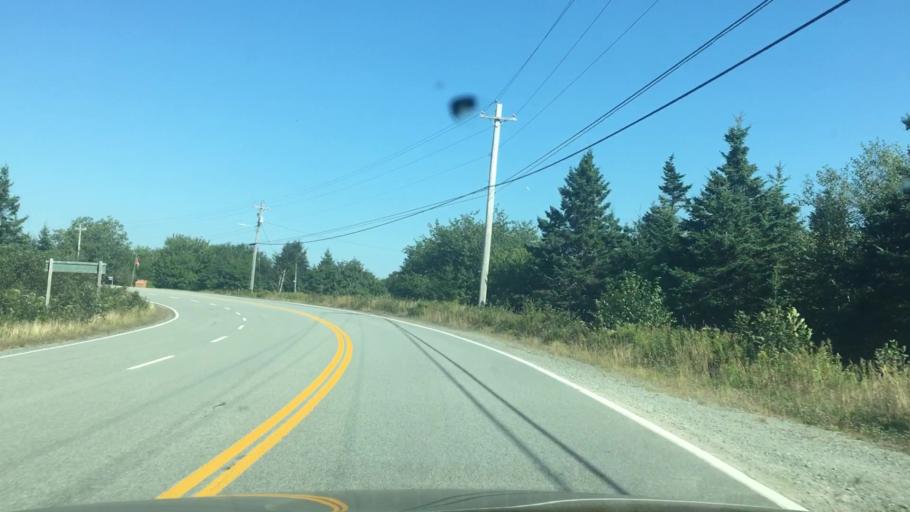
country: CA
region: Nova Scotia
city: New Glasgow
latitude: 44.8152
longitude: -62.6312
